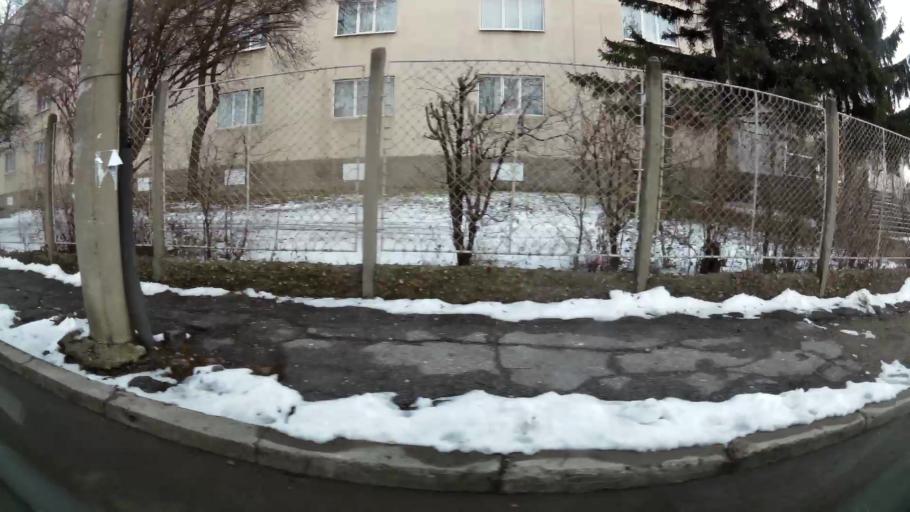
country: BG
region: Sofia-Capital
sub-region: Stolichna Obshtina
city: Sofia
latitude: 42.7161
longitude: 23.3464
